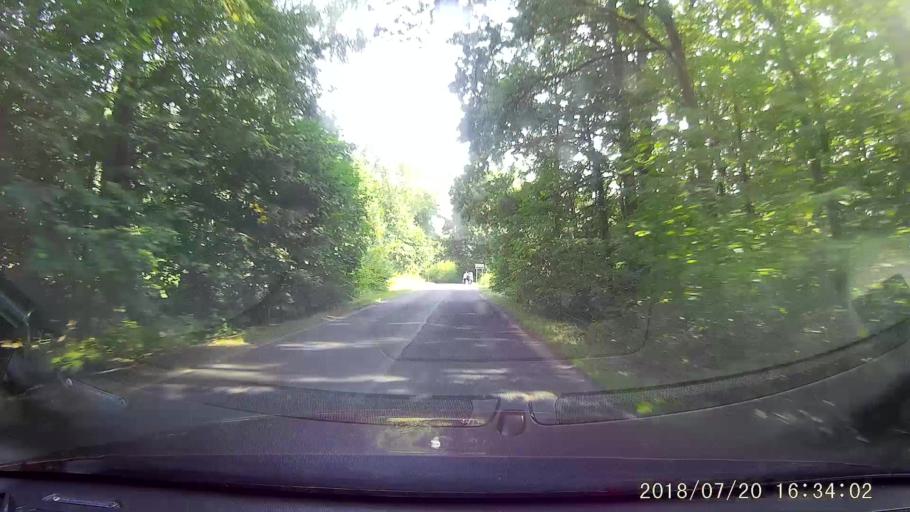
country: PL
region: Lower Silesian Voivodeship
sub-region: Powiat zgorzelecki
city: Sulikow
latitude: 51.0848
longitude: 15.0981
